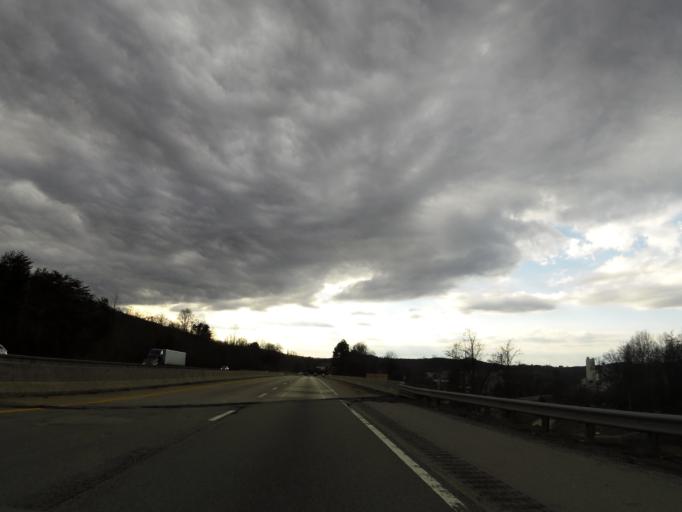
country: US
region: Tennessee
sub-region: Cumberland County
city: Fairfield Glade
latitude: 35.9031
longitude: -84.8602
